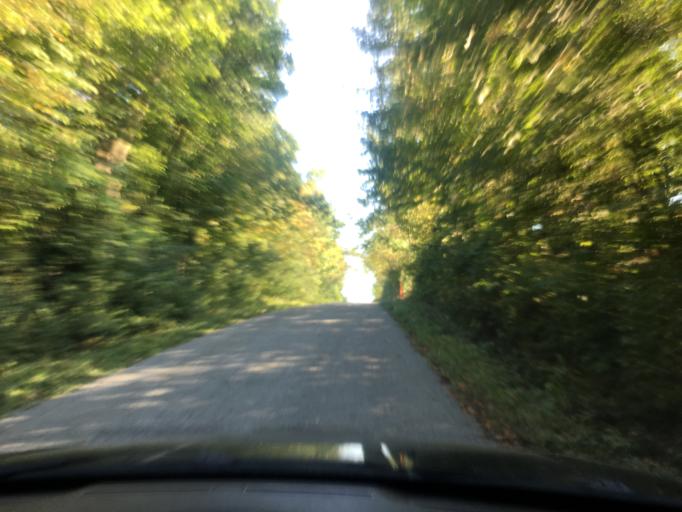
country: US
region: Ohio
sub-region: Logan County
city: West Liberty
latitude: 40.2543
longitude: -83.6626
